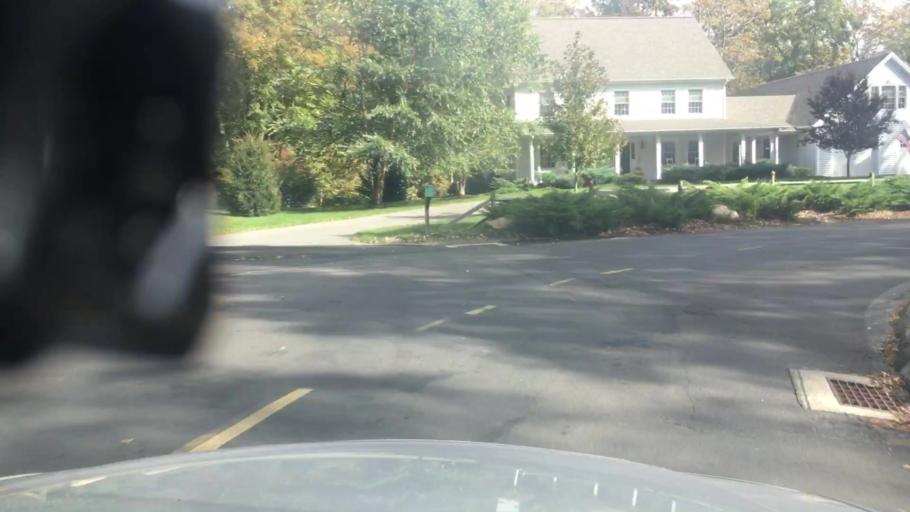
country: US
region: Connecticut
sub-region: Middlesex County
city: Essex Village
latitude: 41.3606
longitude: -72.4063
